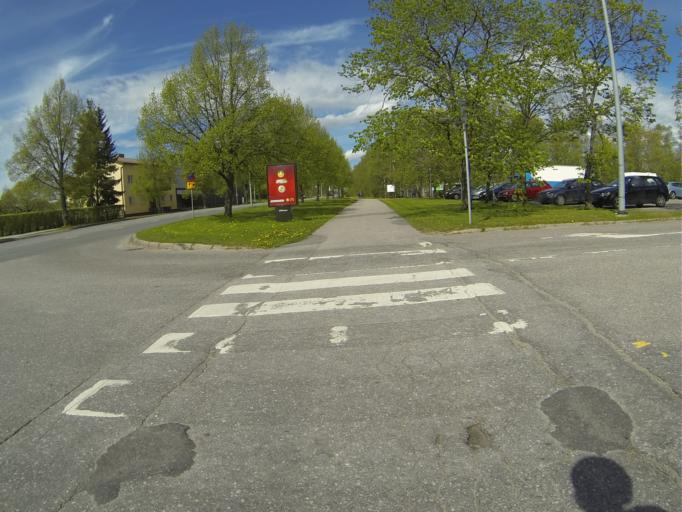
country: FI
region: Varsinais-Suomi
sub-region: Salo
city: Salo
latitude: 60.3796
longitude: 23.1363
